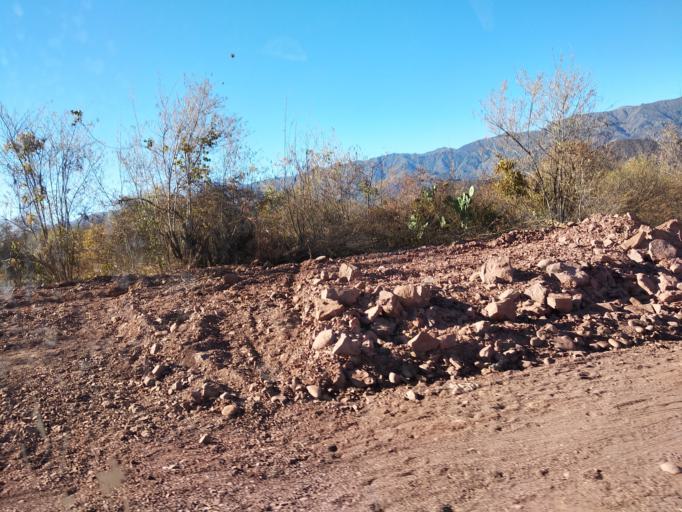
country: BO
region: Cochabamba
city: Mizque
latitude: -18.0757
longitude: -65.7474
